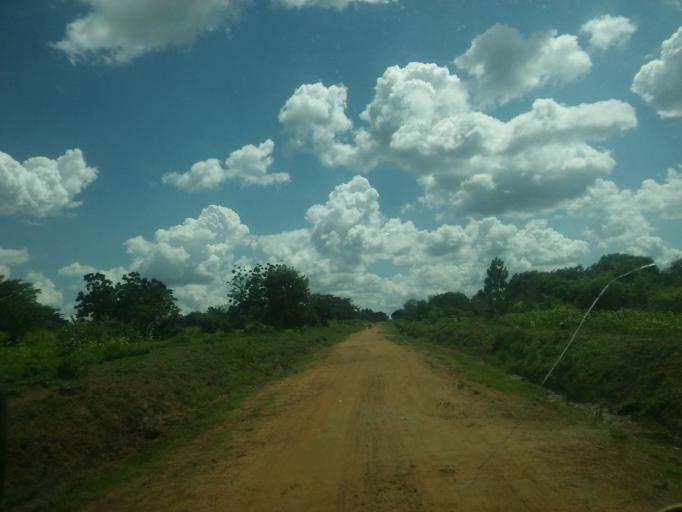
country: UG
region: Eastern Region
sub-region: Pallisa District
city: Pallisa
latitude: 1.1503
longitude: 33.8163
